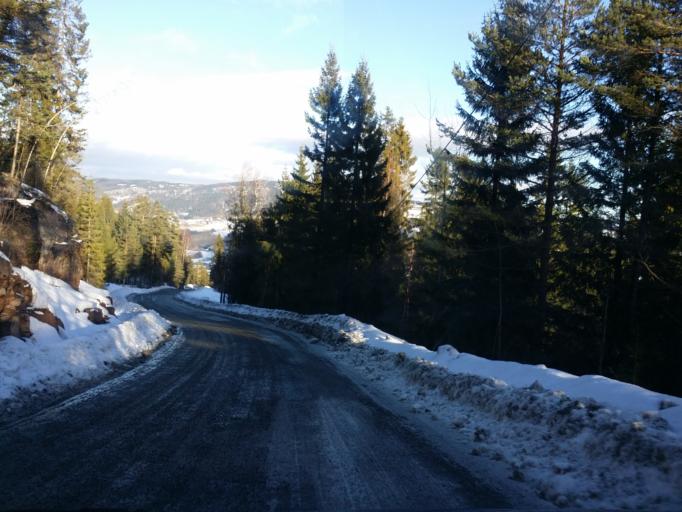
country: NO
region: Buskerud
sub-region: Lier
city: Lierbyen
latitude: 59.8231
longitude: 10.1932
